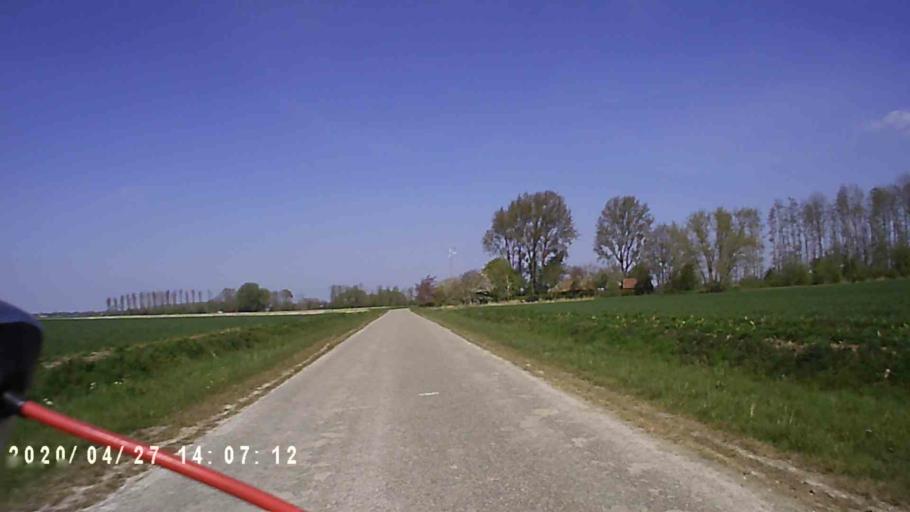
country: NL
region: Groningen
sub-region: Gemeente Zuidhorn
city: Oldehove
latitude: 53.3422
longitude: 6.3936
